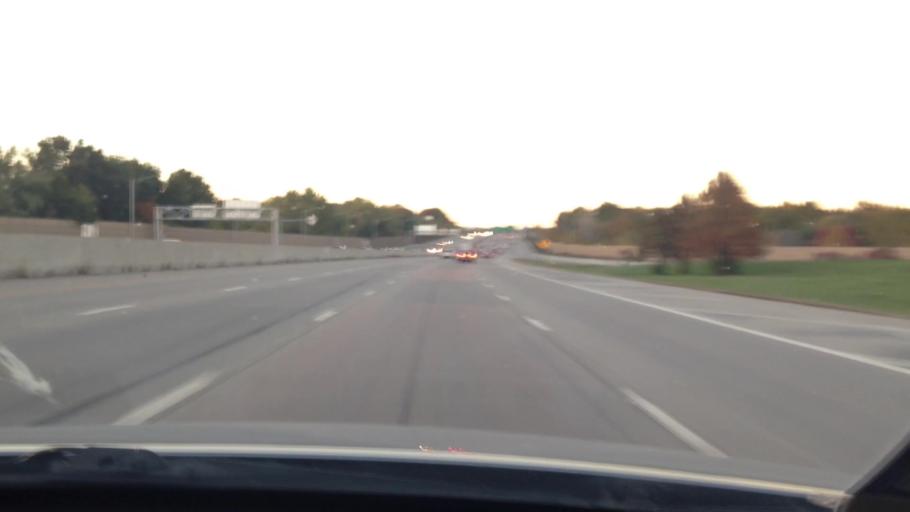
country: US
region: Kansas
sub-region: Johnson County
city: Lenexa
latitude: 38.9435
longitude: -94.7052
